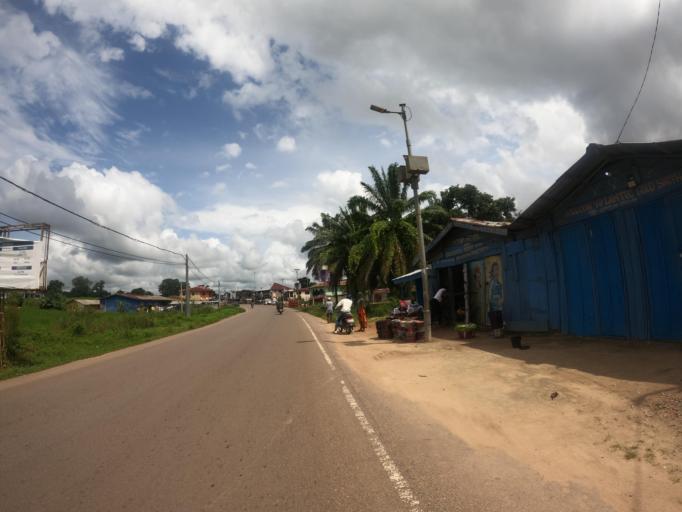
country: SL
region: Northern Province
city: Makeni
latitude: 8.8866
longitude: -12.0529
